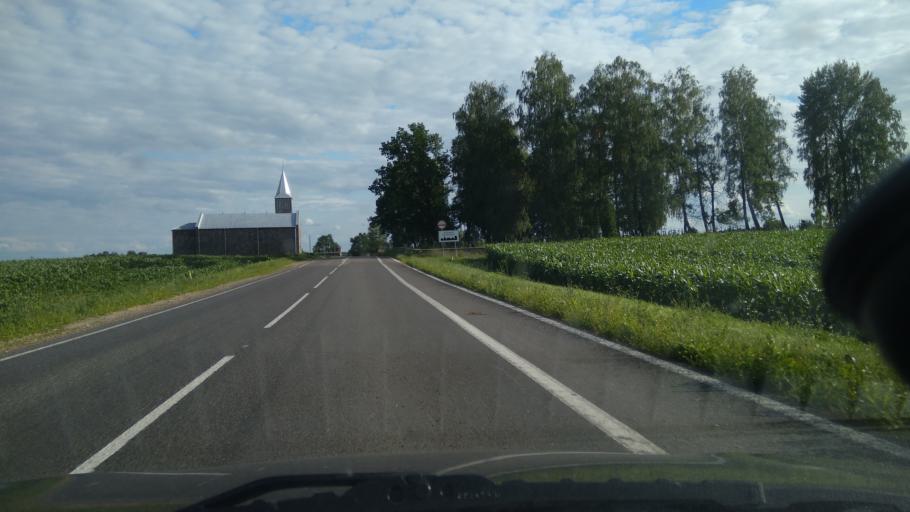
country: BY
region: Grodnenskaya
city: Zel'va
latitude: 53.2768
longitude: 24.6829
